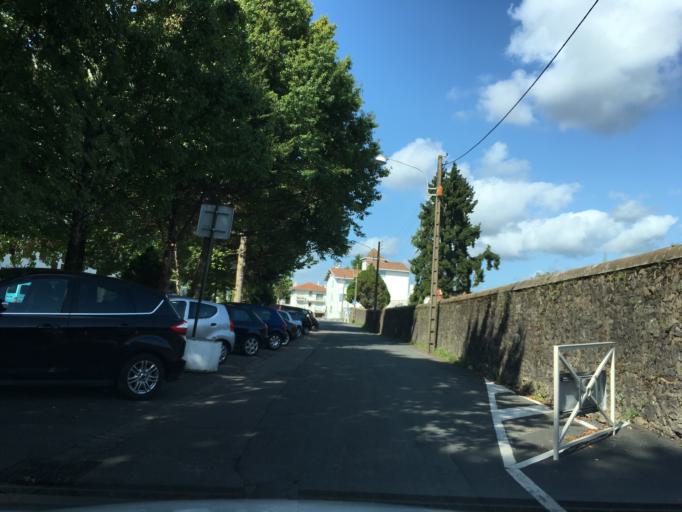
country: FR
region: Aquitaine
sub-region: Departement des Pyrenees-Atlantiques
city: Bayonne
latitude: 43.4853
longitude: -1.4846
